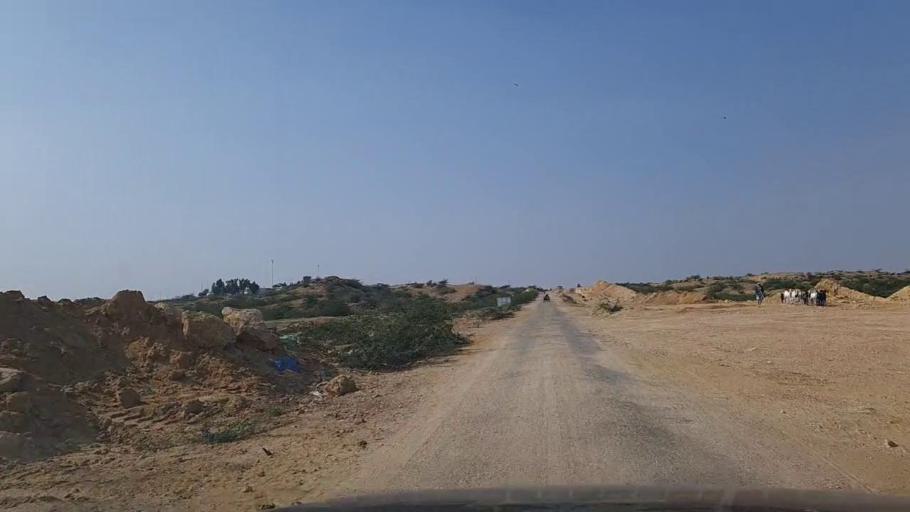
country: PK
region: Sindh
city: Gharo
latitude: 24.7684
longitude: 67.5757
